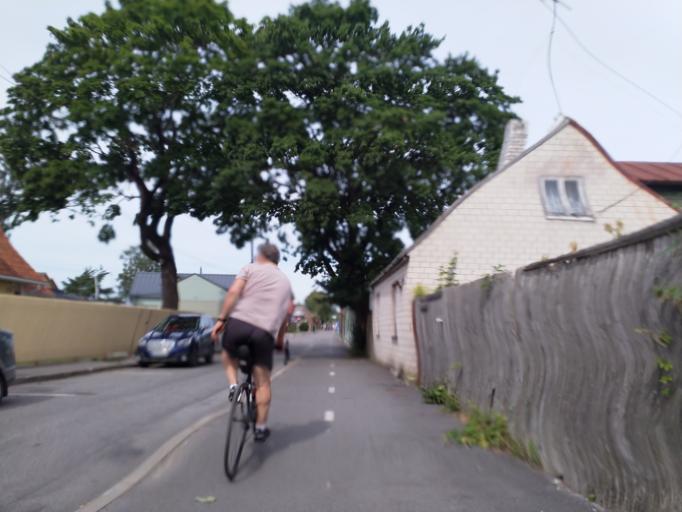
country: EE
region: Paernumaa
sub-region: Paernu linn
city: Parnu
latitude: 58.3776
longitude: 24.5230
